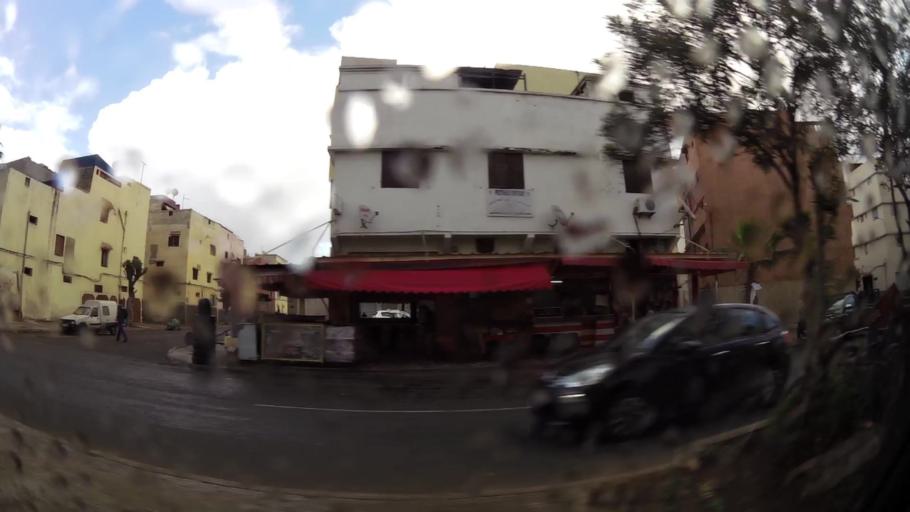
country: MA
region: Grand Casablanca
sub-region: Mohammedia
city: Mohammedia
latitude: 33.6842
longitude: -7.3867
